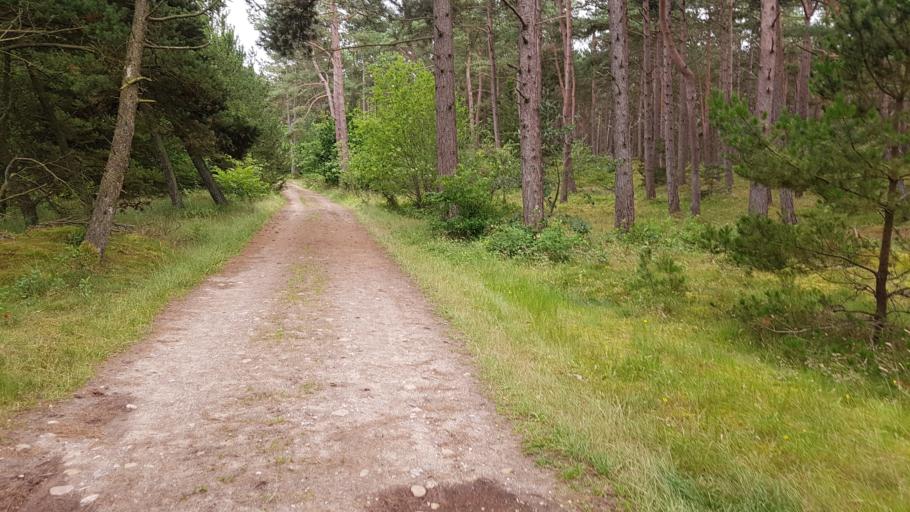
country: DE
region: Schleswig-Holstein
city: List
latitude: 55.0994
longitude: 8.5294
